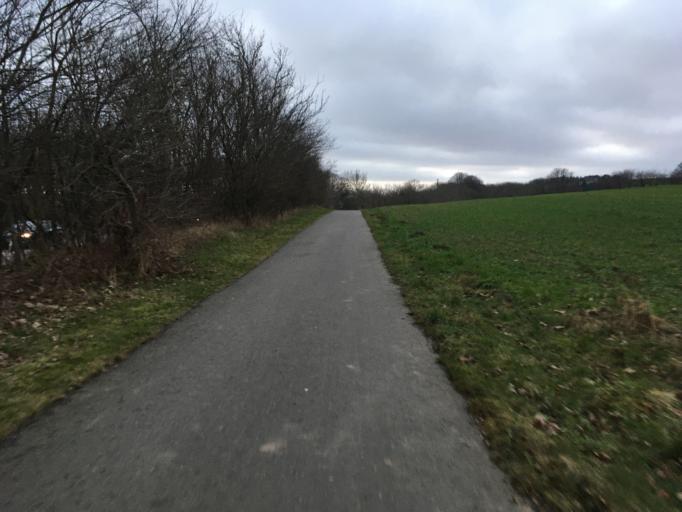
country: DE
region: Mecklenburg-Vorpommern
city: Sassnitz
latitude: 54.5094
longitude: 13.5996
